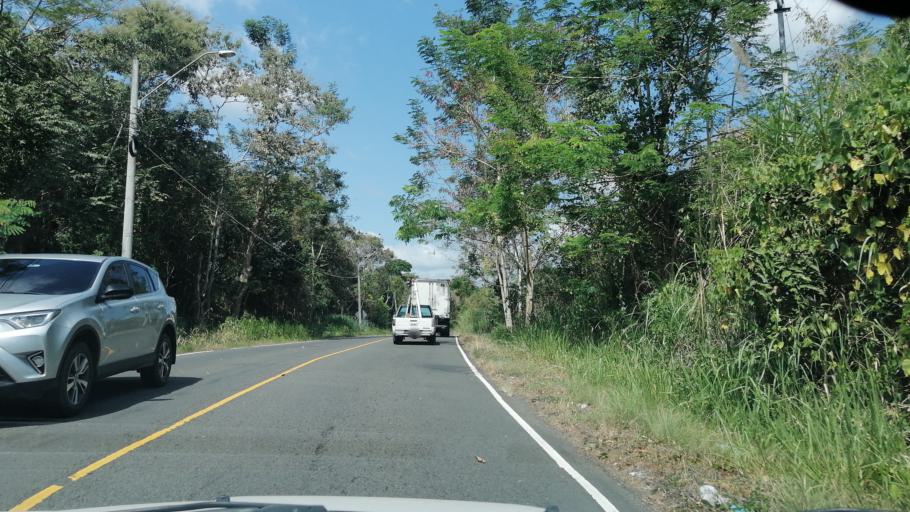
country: PA
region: Panama
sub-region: Distrito de Panama
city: Ancon
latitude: 8.9288
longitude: -79.5724
